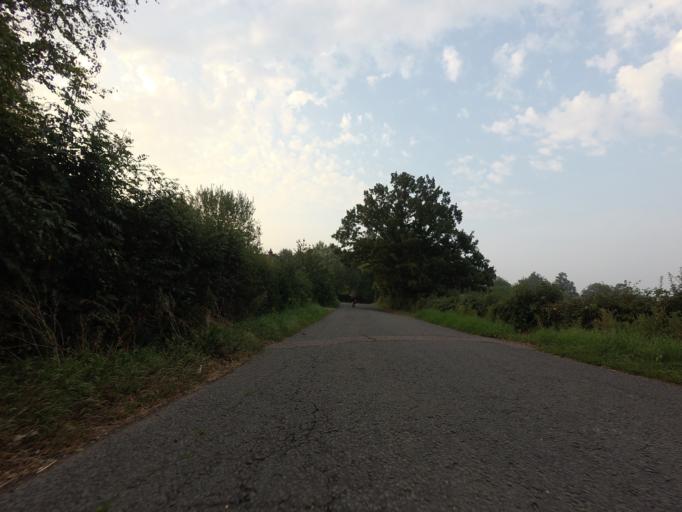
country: GB
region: England
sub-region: Kent
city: Lenham
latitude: 51.1666
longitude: 0.7361
